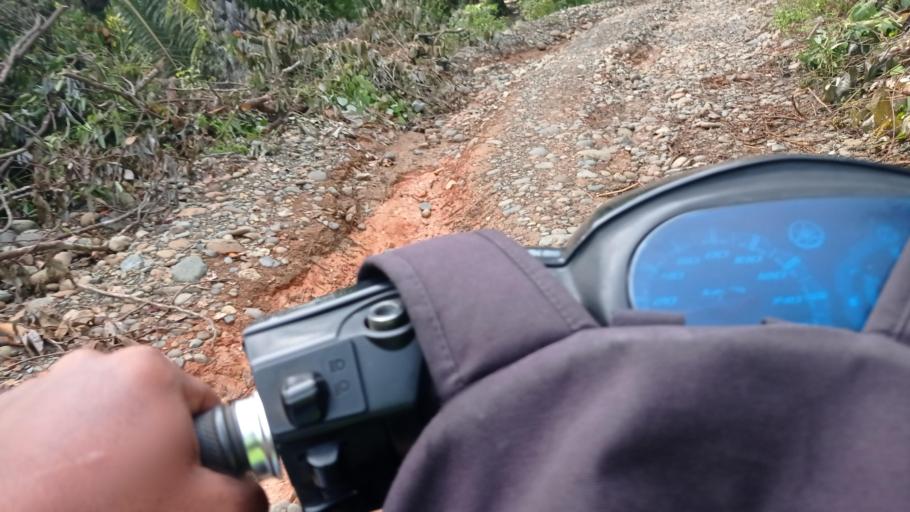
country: ID
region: Bengkulu
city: Ipuh
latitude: -2.6643
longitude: 101.2701
